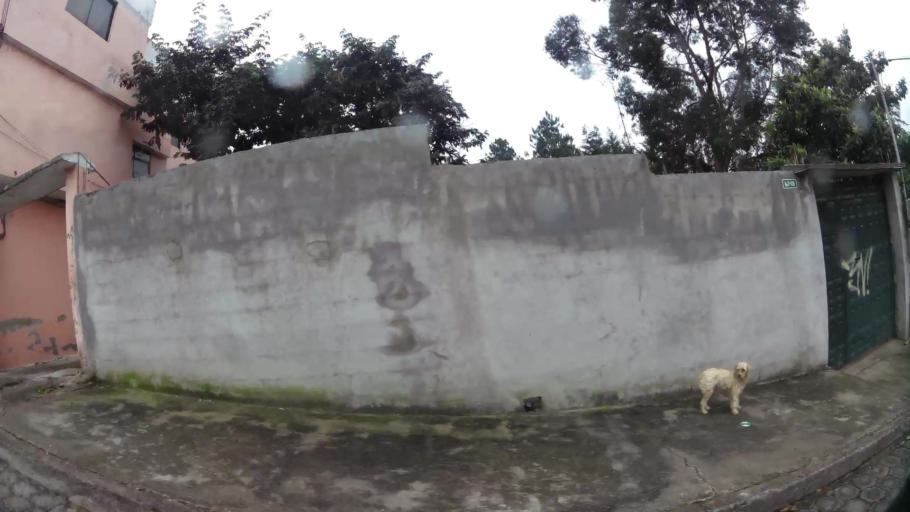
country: EC
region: Pichincha
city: Sangolqui
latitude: -0.2759
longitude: -78.4687
